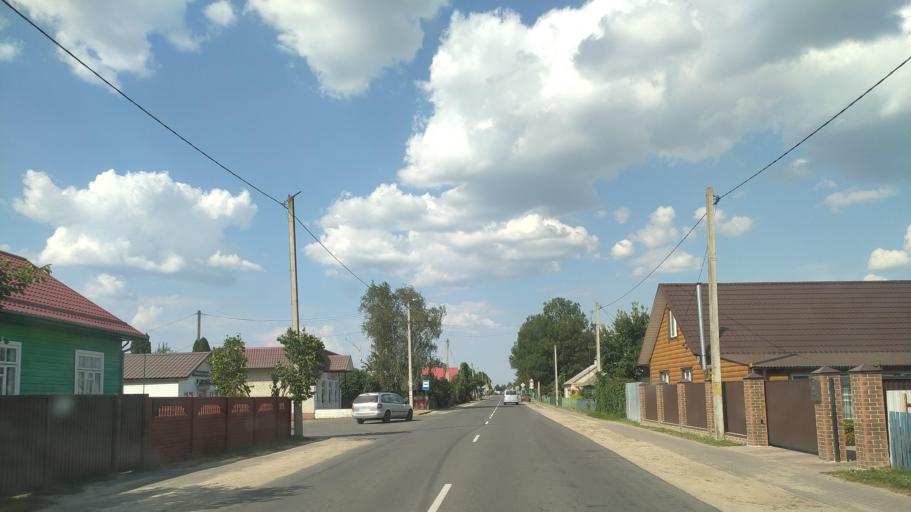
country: BY
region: Brest
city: Drahichyn
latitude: 52.1916
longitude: 25.1470
